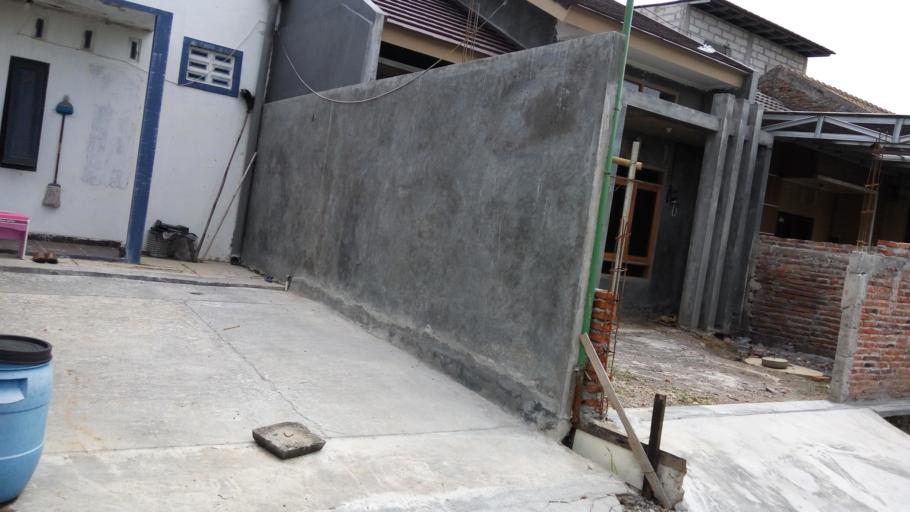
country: ID
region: Central Java
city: Mranggen
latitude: -7.0410
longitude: 110.4814
